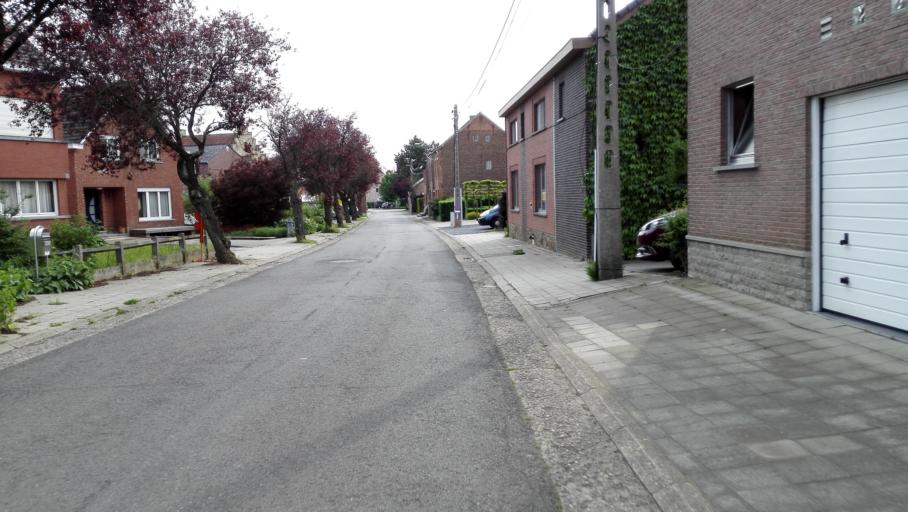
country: BE
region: Flanders
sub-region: Provincie Vlaams-Brabant
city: Holsbeek
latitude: 50.9044
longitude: 4.7406
